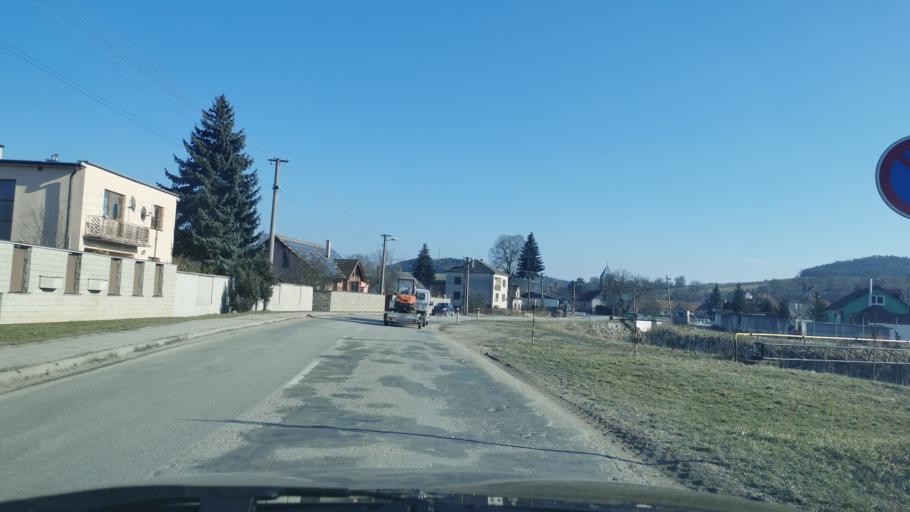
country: SK
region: Trenciansky
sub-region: Okres Myjava
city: Myjava
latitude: 48.7478
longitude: 17.5298
